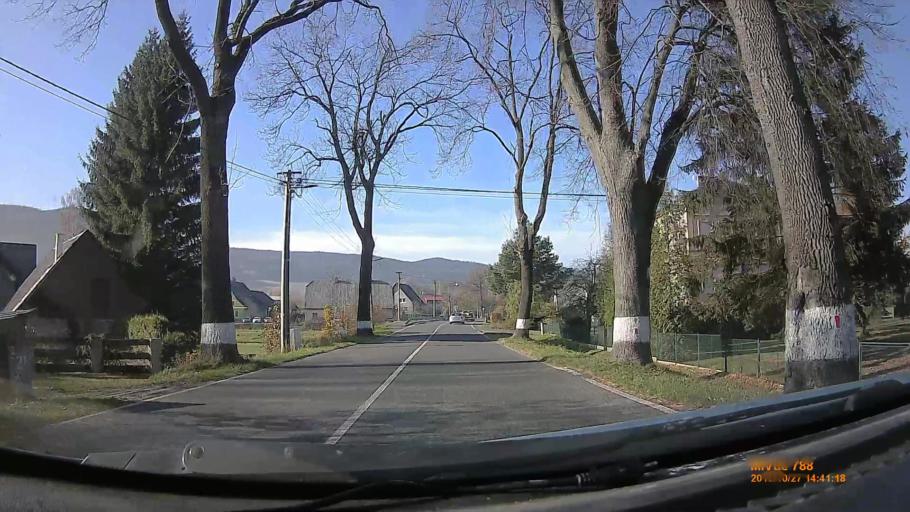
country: CZ
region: Pardubicky
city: Cervena Voda
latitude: 50.0170
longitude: 16.7466
